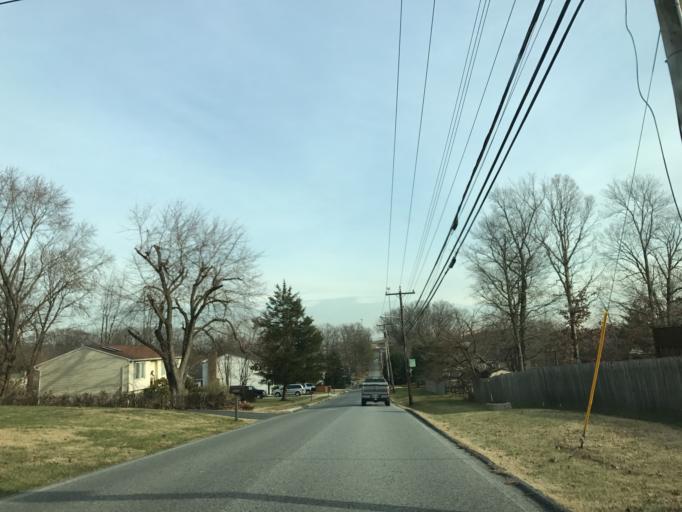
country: US
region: Maryland
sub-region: Baltimore County
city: White Marsh
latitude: 39.3835
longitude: -76.4511
